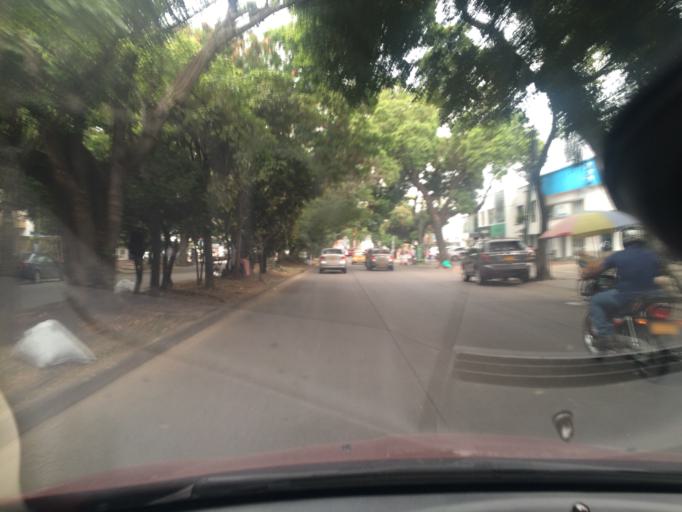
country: CO
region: Valle del Cauca
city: Cali
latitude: 3.4185
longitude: -76.5452
